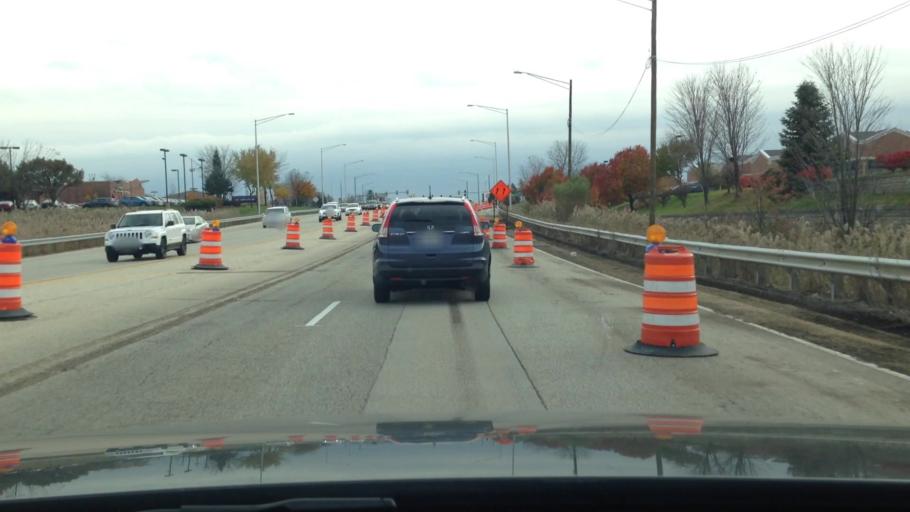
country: US
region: Illinois
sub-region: McHenry County
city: Lake in the Hills
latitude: 42.1645
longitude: -88.3355
